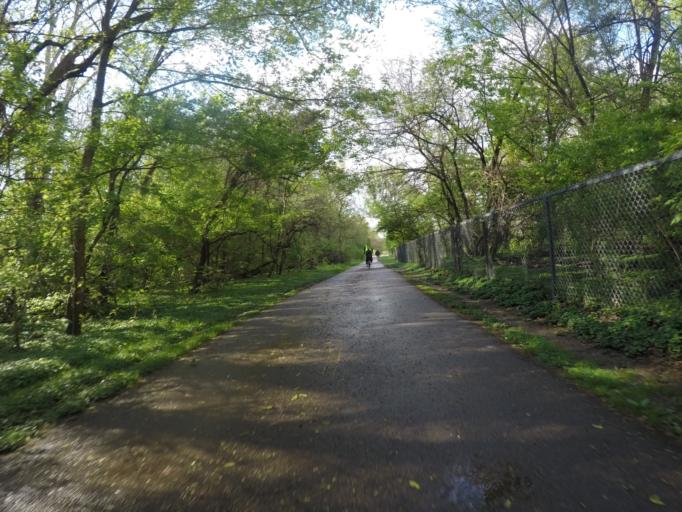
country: US
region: Ohio
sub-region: Franklin County
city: Grandview Heights
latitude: 40.0237
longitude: -83.0215
